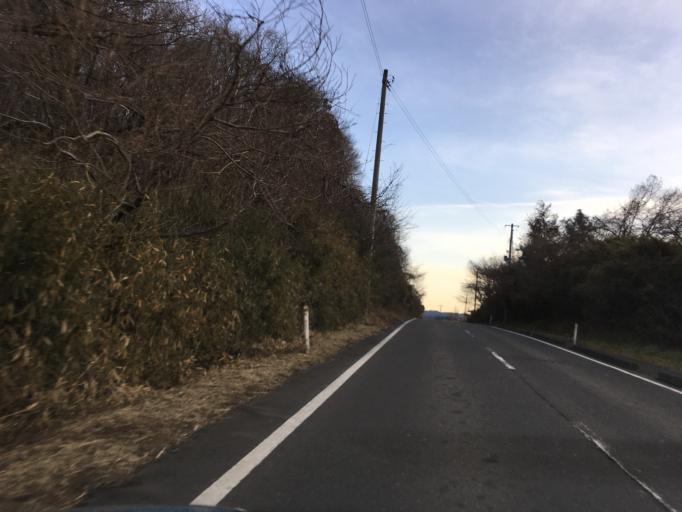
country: JP
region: Miyagi
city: Kogota
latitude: 38.6652
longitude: 141.0721
